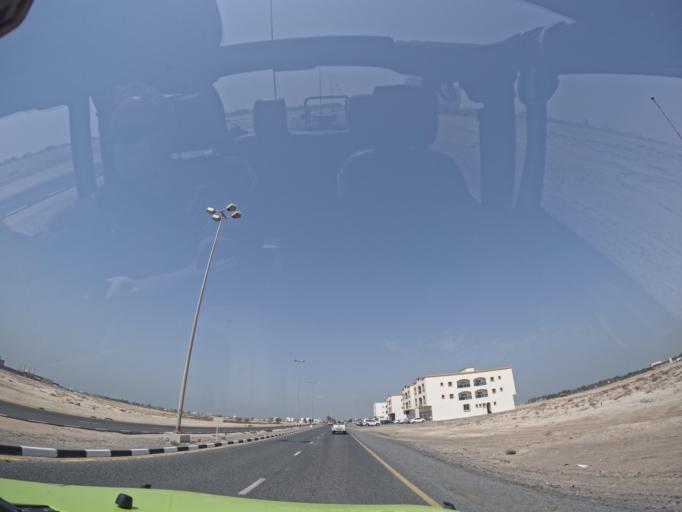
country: AE
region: Umm al Qaywayn
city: Umm al Qaywayn
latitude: 25.5190
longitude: 55.5549
